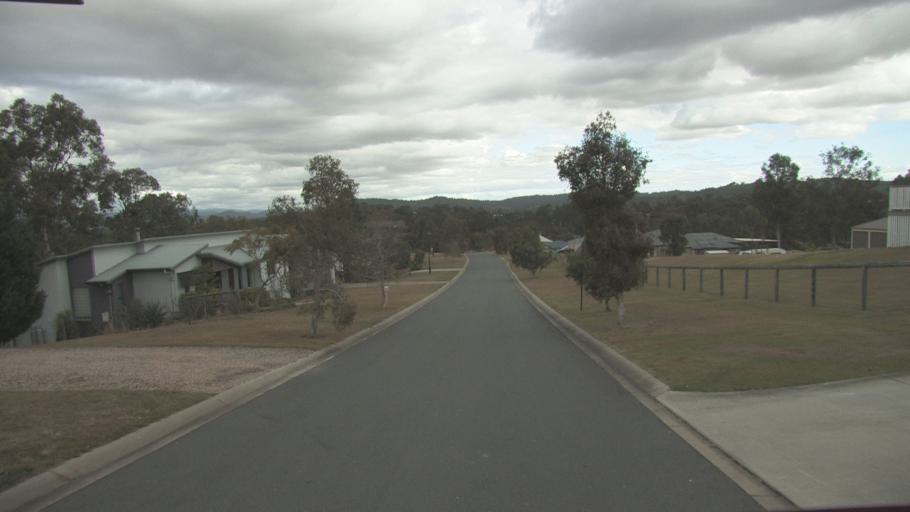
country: AU
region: Queensland
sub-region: Logan
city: Cedar Vale
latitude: -27.8685
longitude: 153.0792
